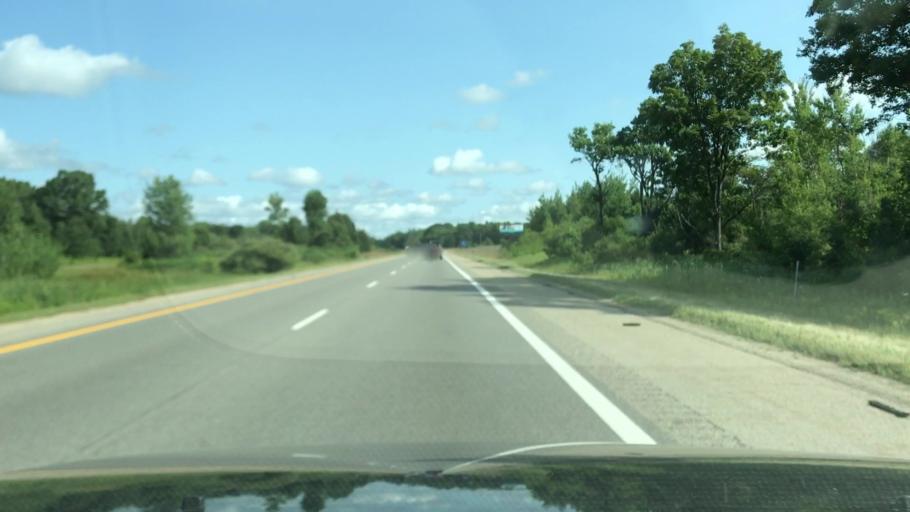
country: US
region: Michigan
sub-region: Kent County
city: Cedar Springs
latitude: 43.2723
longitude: -85.5415
